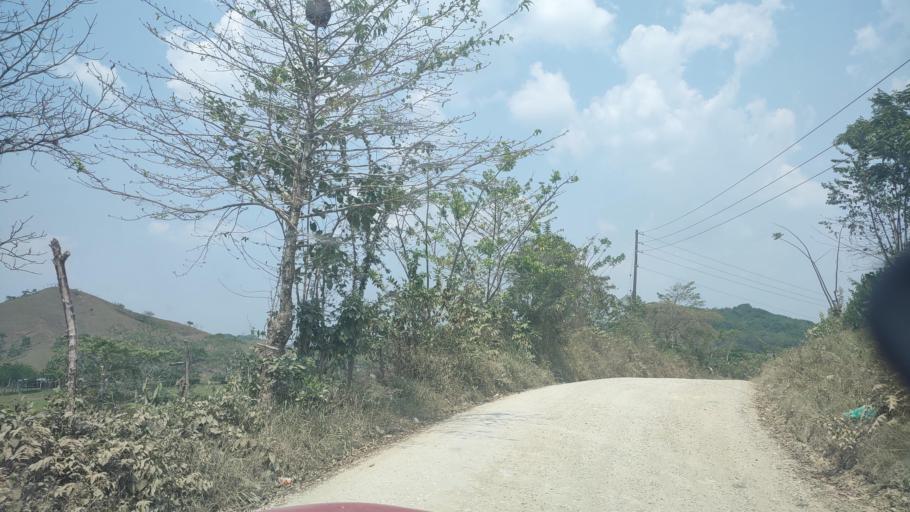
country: MX
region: Tabasco
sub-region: Huimanguillo
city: Francisco Rueda
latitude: 17.6081
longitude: -93.9092
